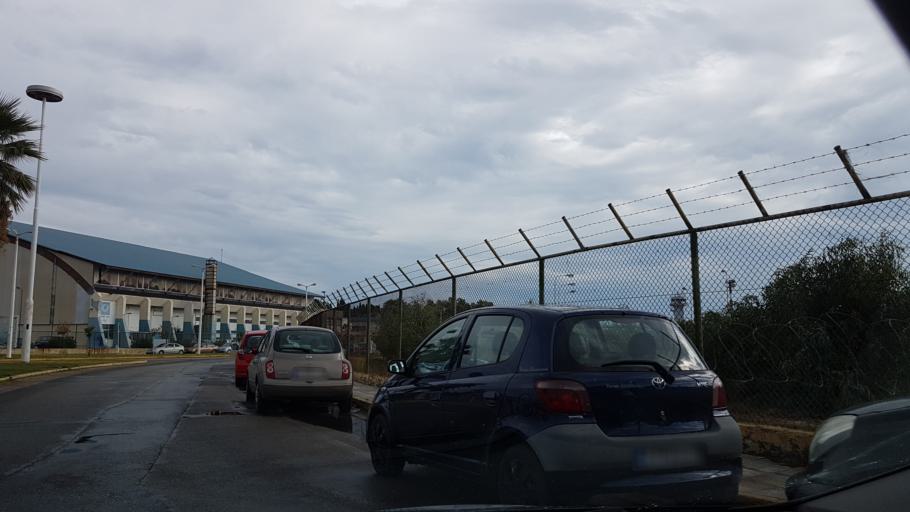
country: GR
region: Ionian Islands
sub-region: Nomos Kerkyras
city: Kerkyra
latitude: 39.6116
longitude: 19.9135
